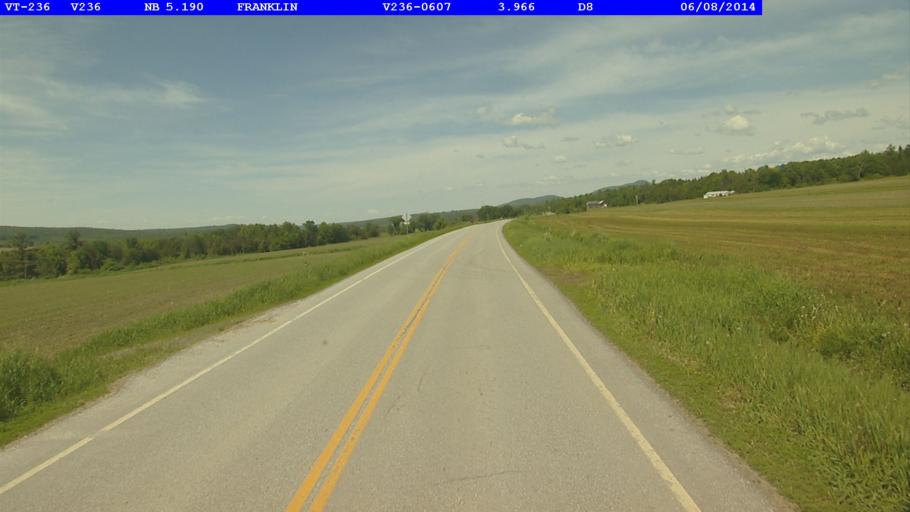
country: US
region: Vermont
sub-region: Franklin County
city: Enosburg Falls
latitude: 44.9817
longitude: -72.8423
